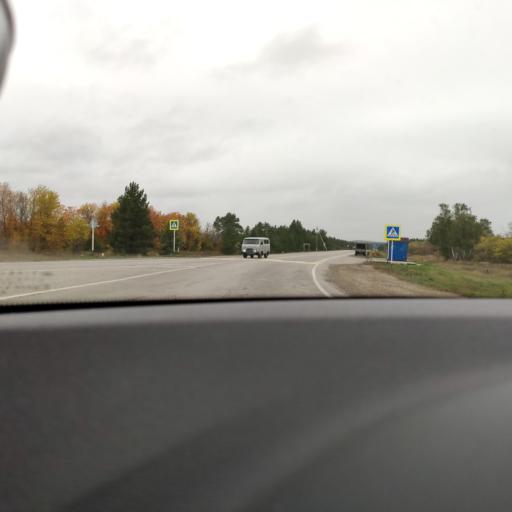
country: RU
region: Samara
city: Mirnyy
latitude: 53.5242
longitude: 50.3176
